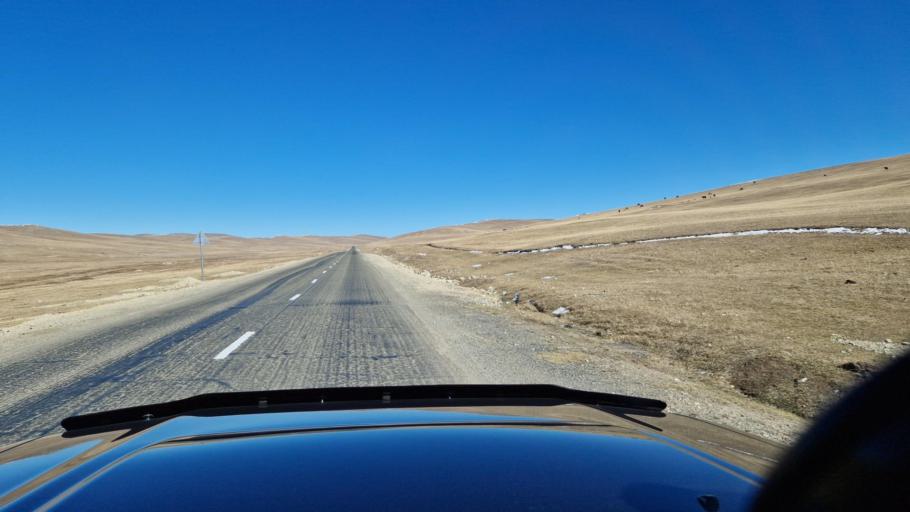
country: MN
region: Hentiy
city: Modot
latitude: 47.7690
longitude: 108.6498
